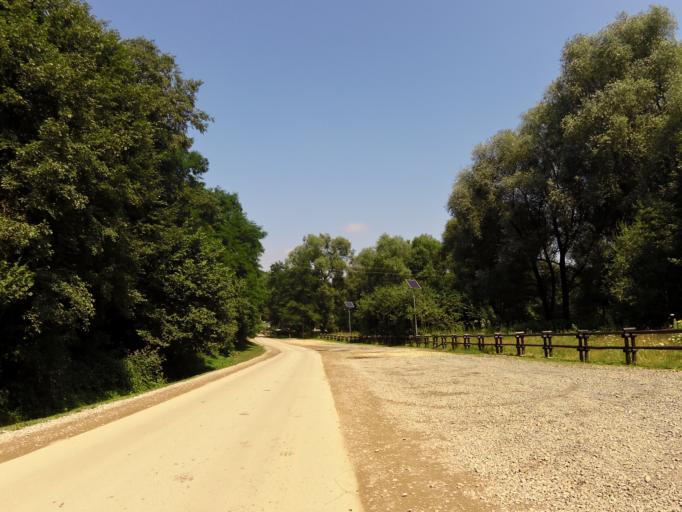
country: PL
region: Silesian Voivodeship
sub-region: Powiat zywiecki
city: Cisiec
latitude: 49.6015
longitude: 19.1041
